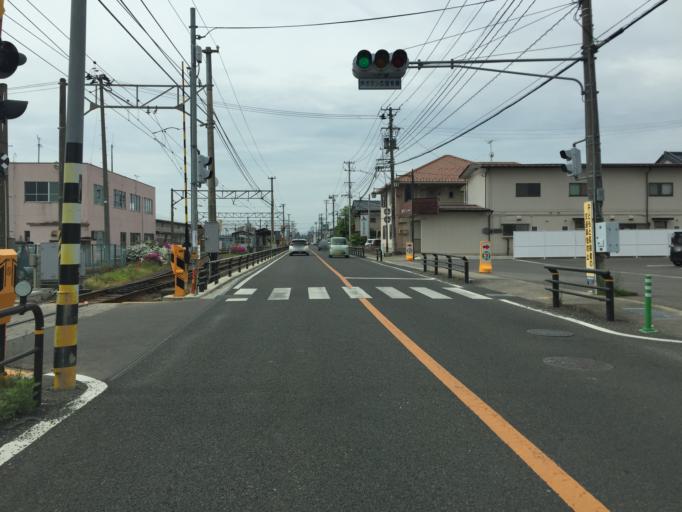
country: JP
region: Fukushima
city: Fukushima-shi
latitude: 37.7973
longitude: 140.4412
